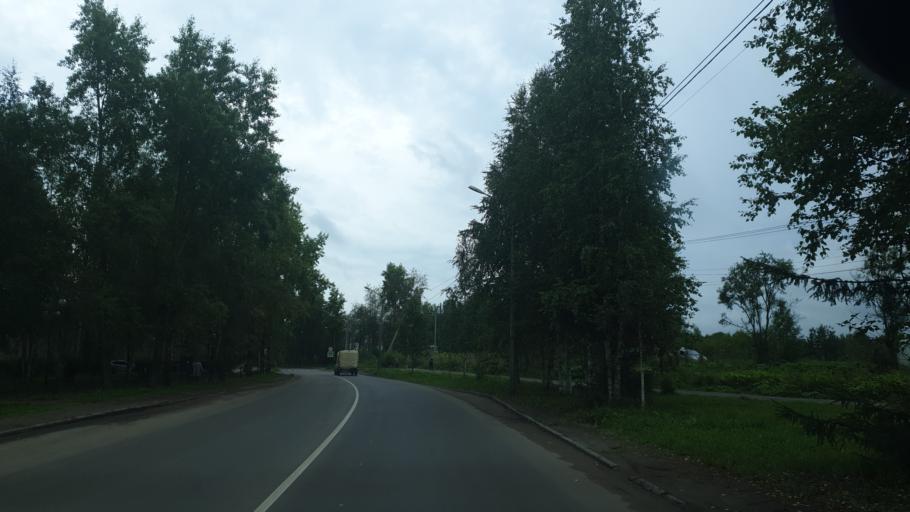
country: RU
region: Komi Republic
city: Ezhva
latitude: 61.7932
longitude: 50.7410
